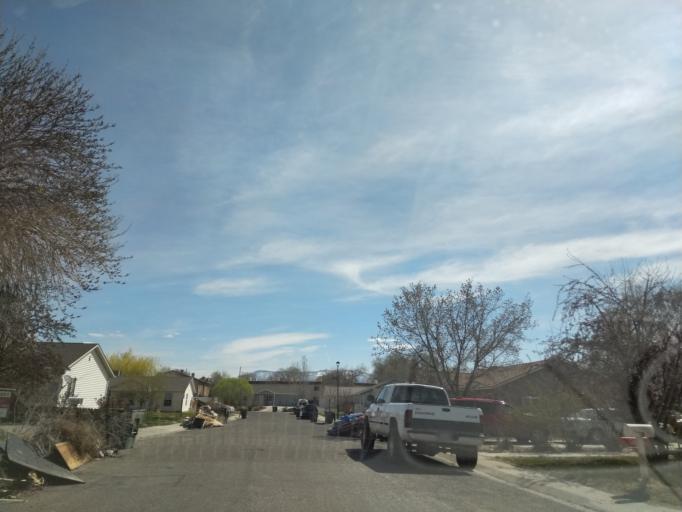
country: US
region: Colorado
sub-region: Mesa County
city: Grand Junction
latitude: 39.0796
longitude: -108.5272
